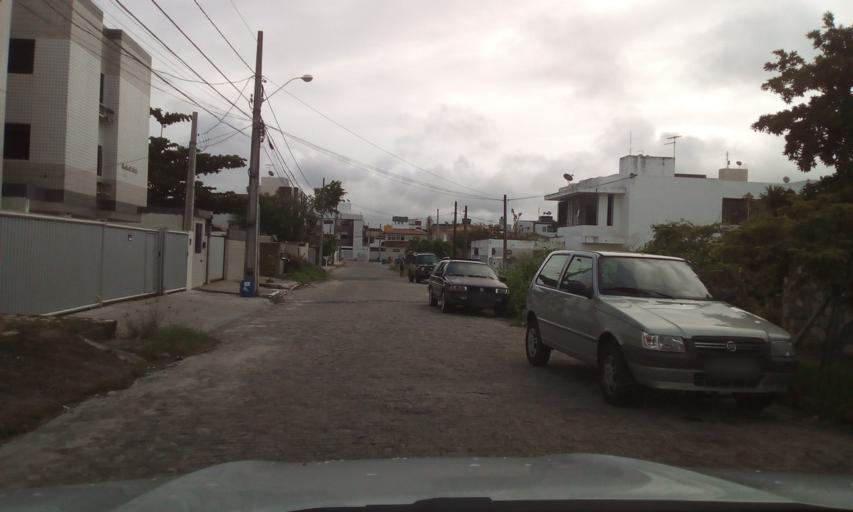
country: BR
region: Paraiba
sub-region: Joao Pessoa
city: Joao Pessoa
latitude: -7.0609
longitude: -34.8440
